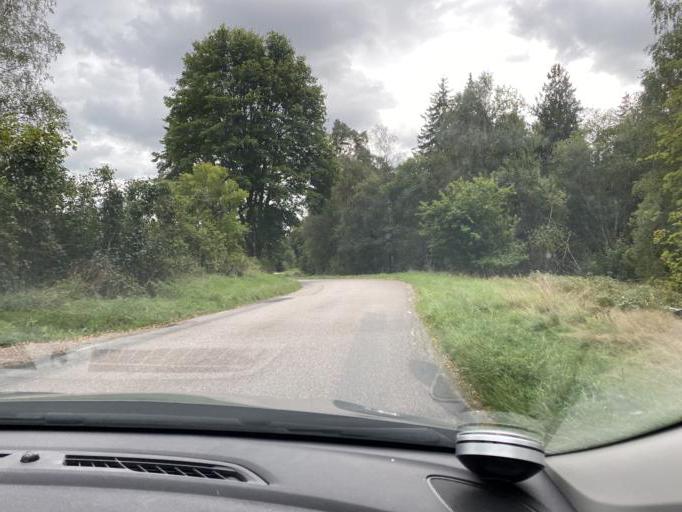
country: SE
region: Kronoberg
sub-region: Markaryds Kommun
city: Markaryd
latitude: 56.4733
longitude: 13.5664
